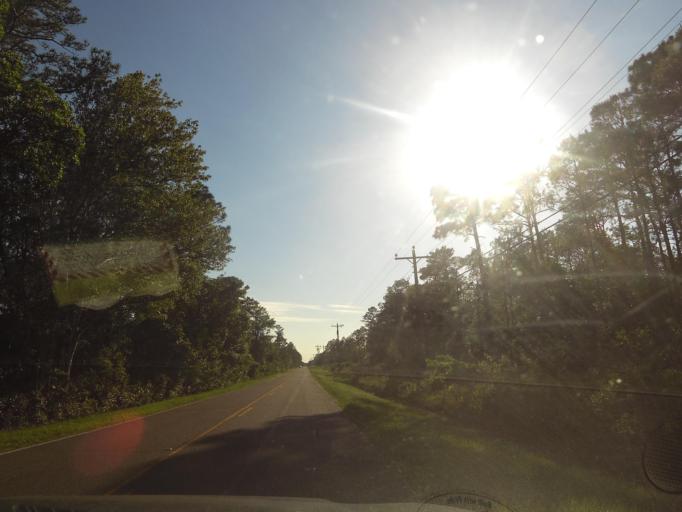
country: US
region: Florida
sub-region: Duval County
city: Atlantic Beach
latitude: 30.4620
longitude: -81.4943
